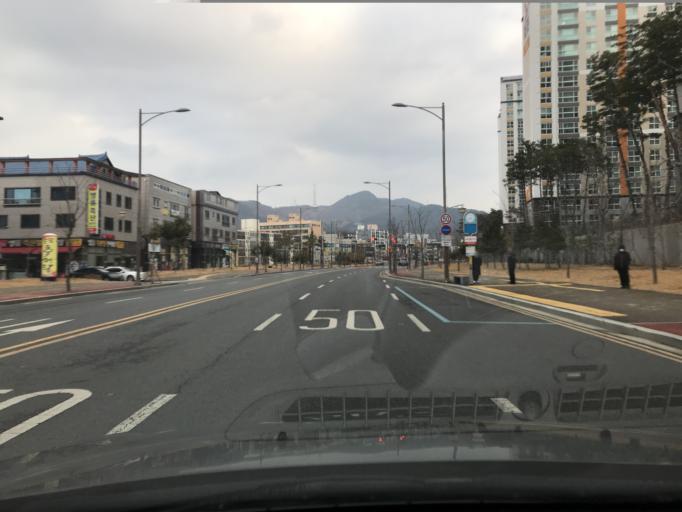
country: KR
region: Daegu
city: Hwawon
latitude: 35.6924
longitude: 128.4496
